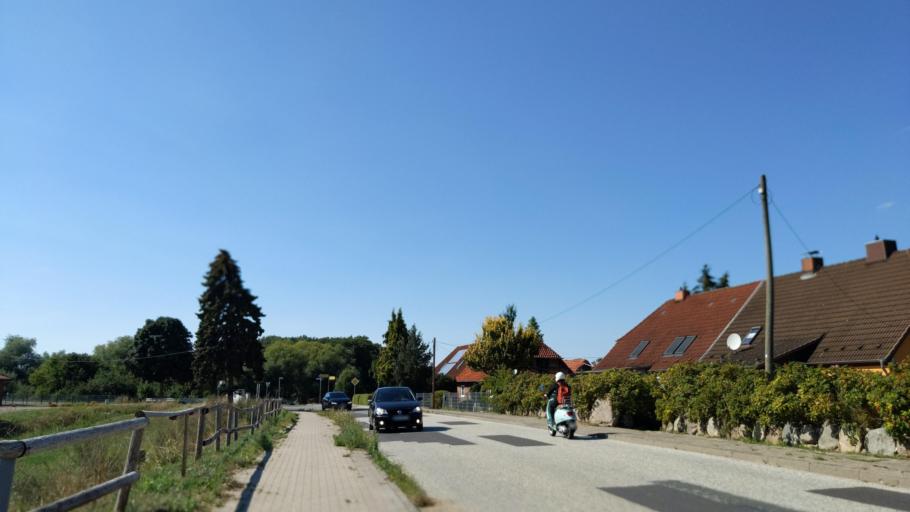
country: DE
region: Mecklenburg-Vorpommern
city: Selmsdorf
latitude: 53.8317
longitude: 10.8702
